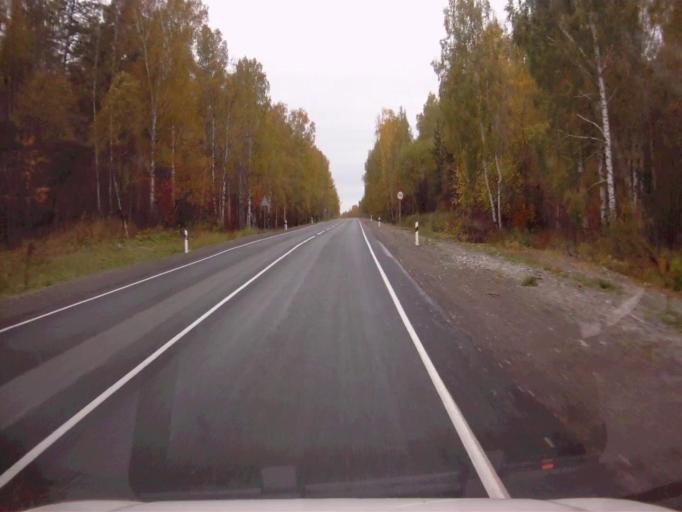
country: RU
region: Chelyabinsk
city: Nyazepetrovsk
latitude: 56.0574
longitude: 59.7346
